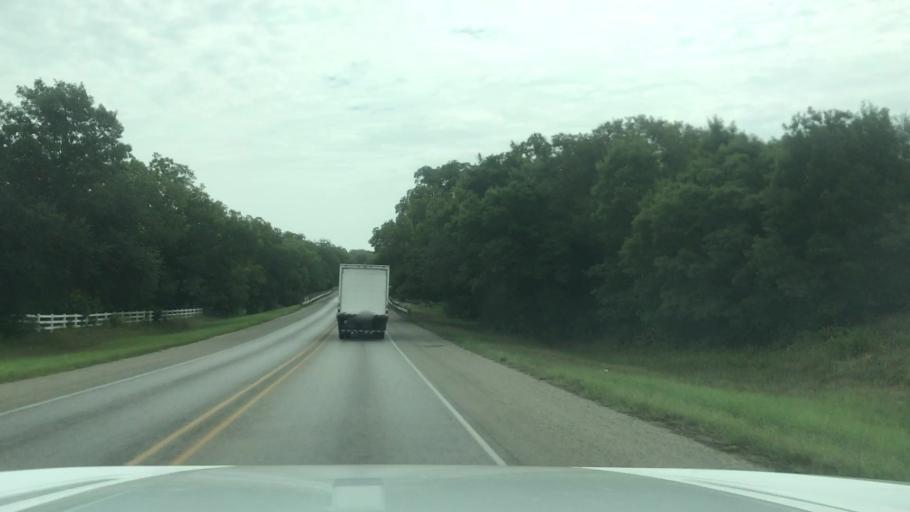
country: US
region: Texas
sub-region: Comanche County
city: De Leon
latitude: 32.1034
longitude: -98.4830
